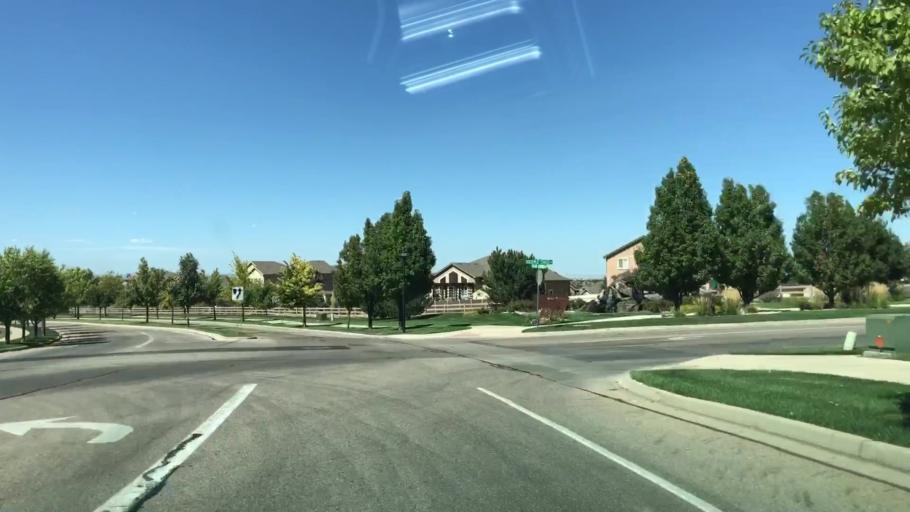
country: US
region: Colorado
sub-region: Weld County
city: Windsor
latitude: 40.4415
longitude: -104.9679
